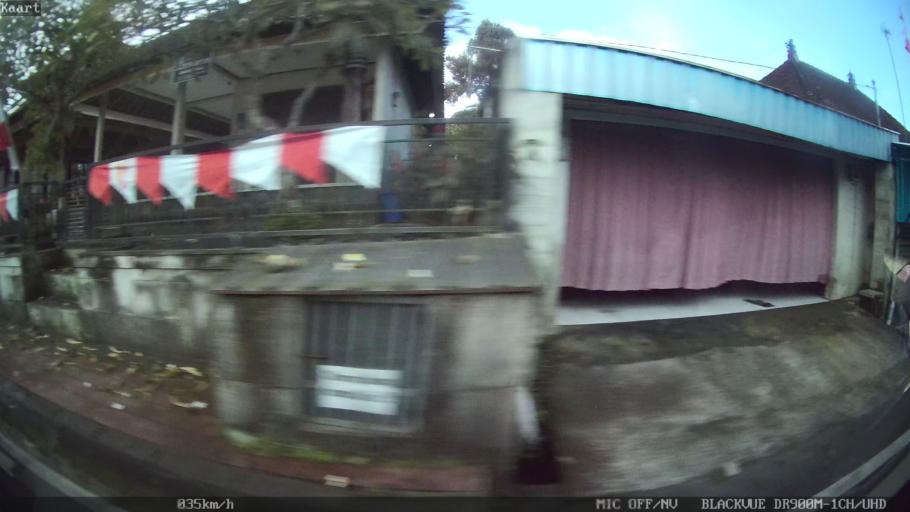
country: ID
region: Bali
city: Banjar Pesalakan
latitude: -8.4929
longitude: 115.2978
